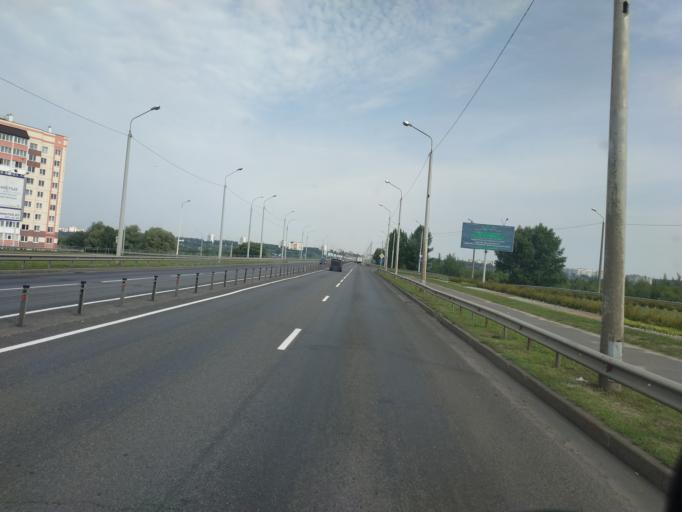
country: BY
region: Mogilev
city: Mahilyow
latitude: 53.8840
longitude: 30.3802
